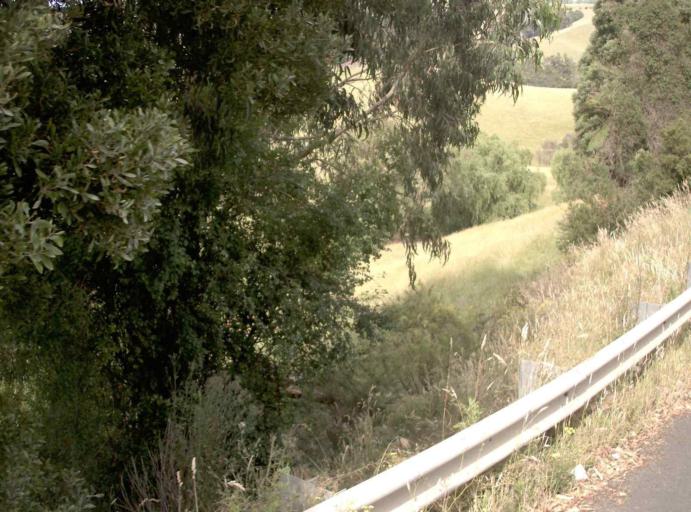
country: AU
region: Victoria
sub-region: Latrobe
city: Moe
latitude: -38.2336
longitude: 146.1678
